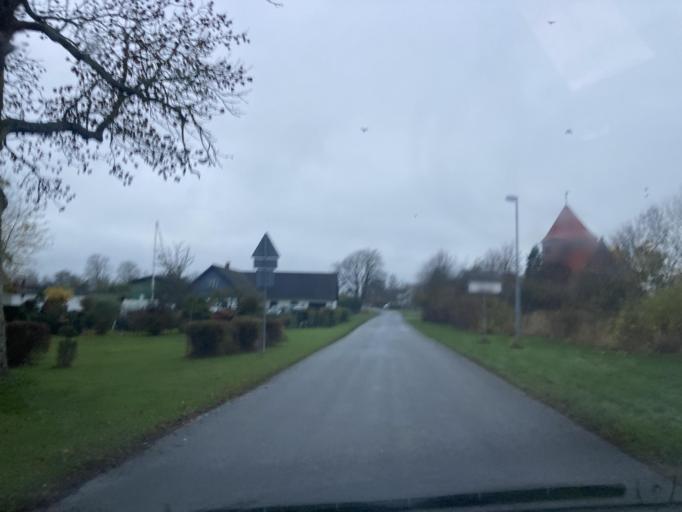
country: DK
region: Zealand
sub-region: Lolland Kommune
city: Holeby
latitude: 54.6787
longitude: 11.4534
